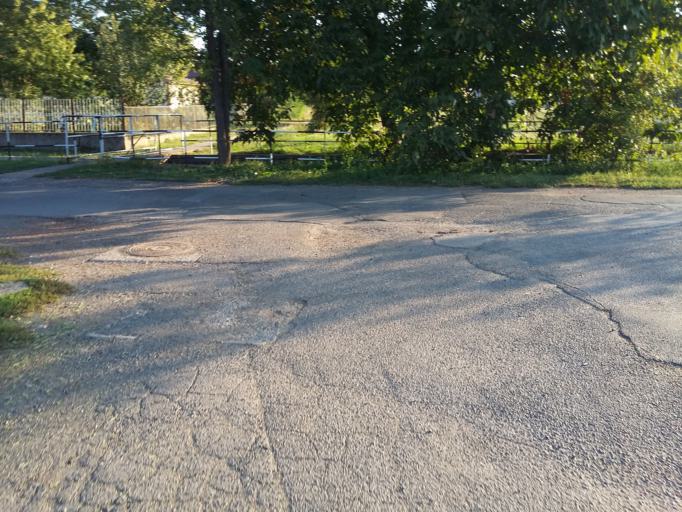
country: HU
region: Borsod-Abauj-Zemplen
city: Bekecs
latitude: 48.1591
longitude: 21.1828
